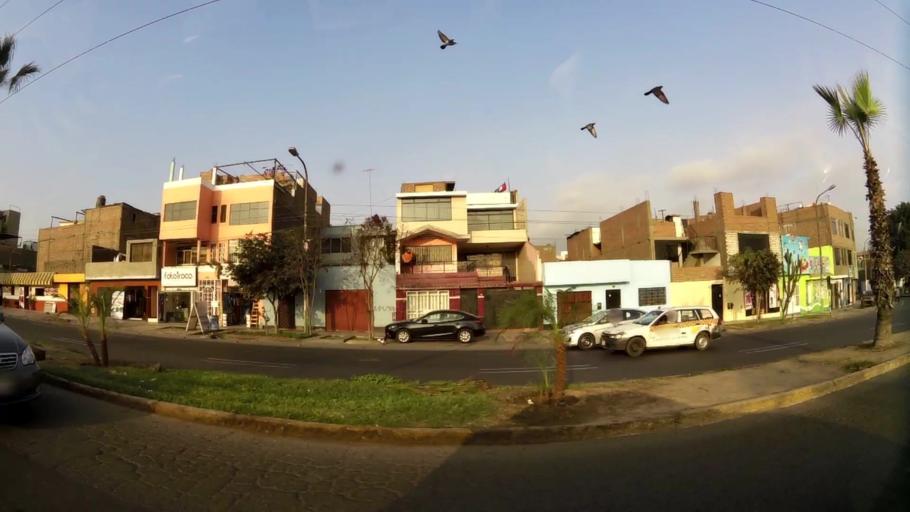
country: PE
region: Lima
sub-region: Lima
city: Independencia
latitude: -11.9860
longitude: -77.0724
